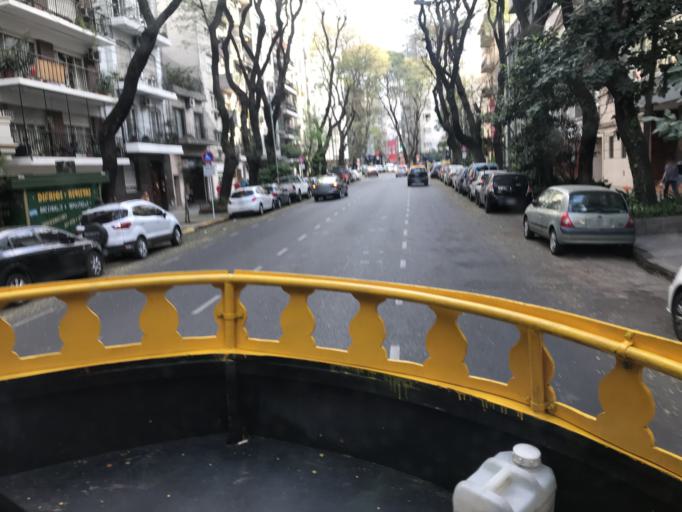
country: AR
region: Buenos Aires F.D.
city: Retiro
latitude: -34.5933
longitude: -58.4136
